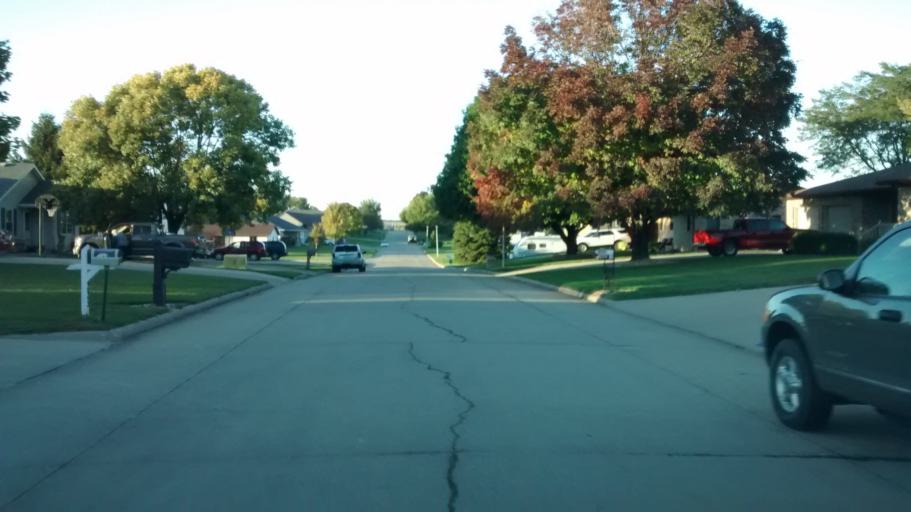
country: US
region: Iowa
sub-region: Woodbury County
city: Moville
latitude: 42.4921
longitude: -96.0666
